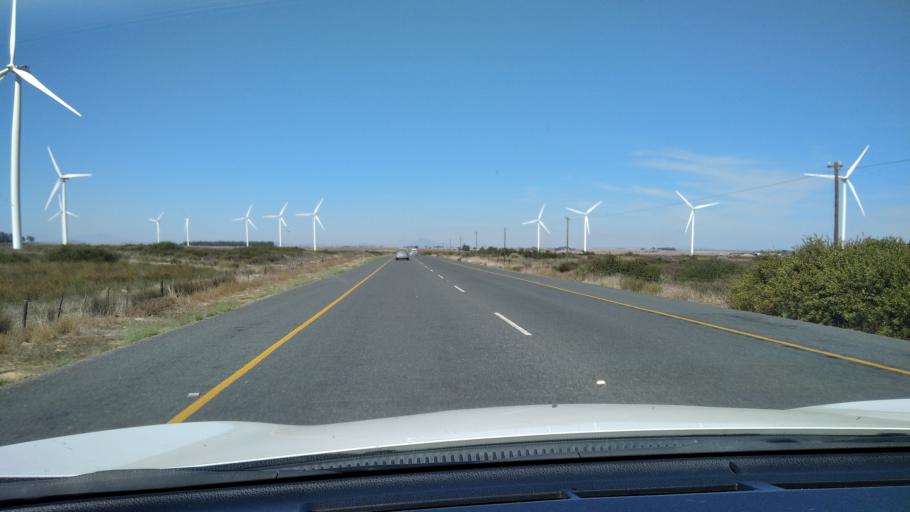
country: ZA
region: Western Cape
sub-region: West Coast District Municipality
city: Moorreesburg
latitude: -33.0822
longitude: 18.3923
